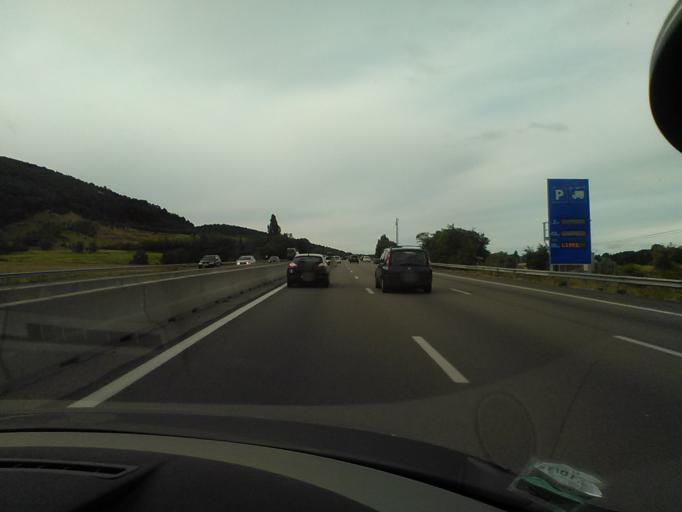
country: FR
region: Rhone-Alpes
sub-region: Departement de la Drome
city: Montboucher-sur-Jabron
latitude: 44.5339
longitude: 4.8026
